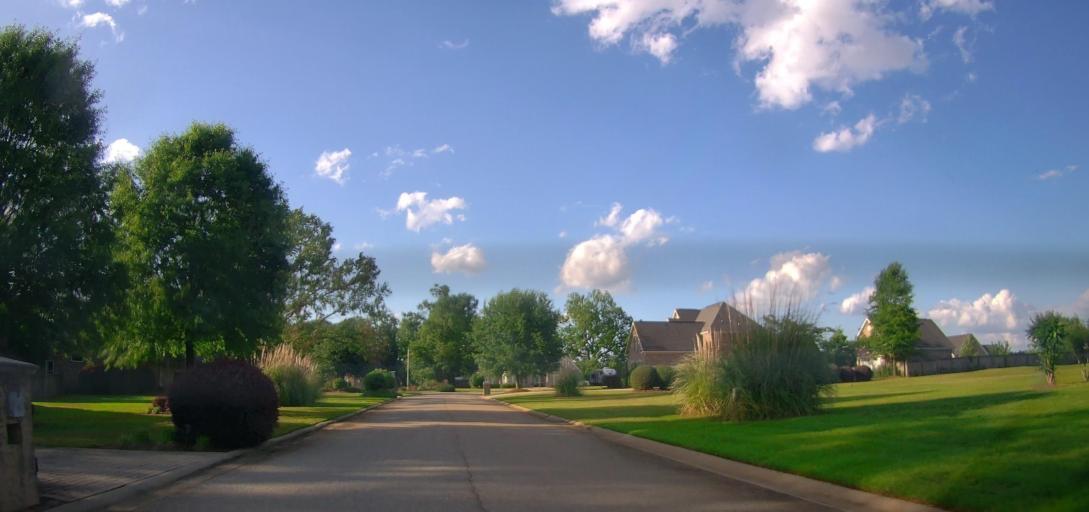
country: US
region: Georgia
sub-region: Peach County
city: Byron
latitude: 32.6463
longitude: -83.7937
